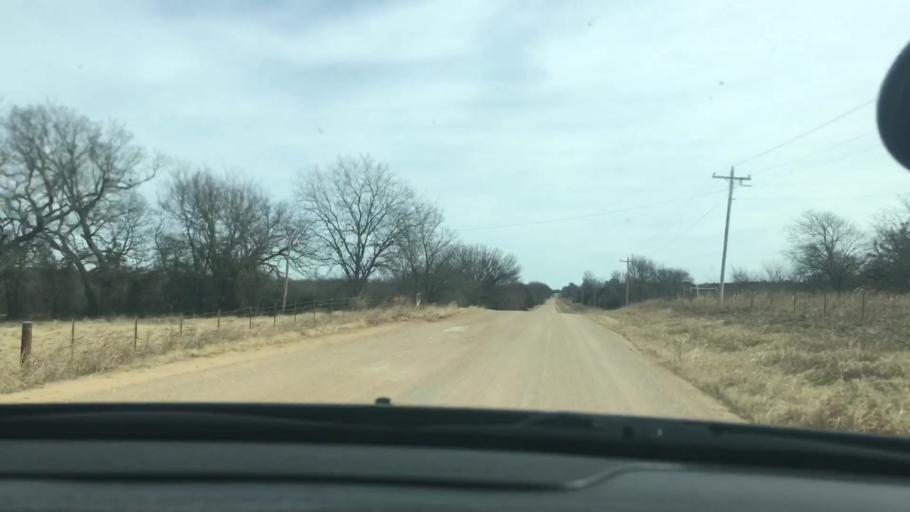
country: US
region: Oklahoma
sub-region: Murray County
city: Sulphur
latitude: 34.4065
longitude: -96.9473
